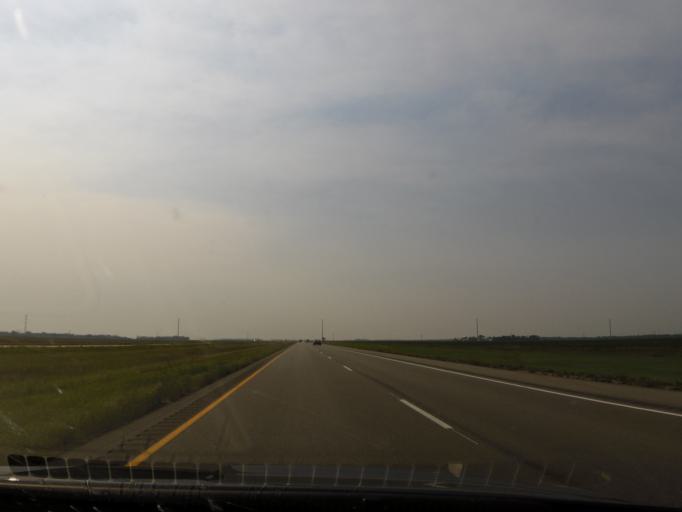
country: US
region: North Dakota
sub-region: Cass County
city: Horace
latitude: 46.6948
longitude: -96.8308
